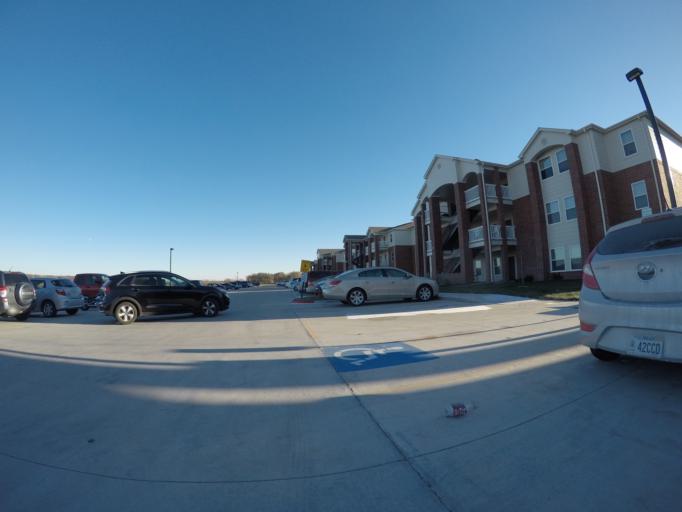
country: US
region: Kansas
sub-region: Riley County
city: Manhattan
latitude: 39.2221
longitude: -96.5627
